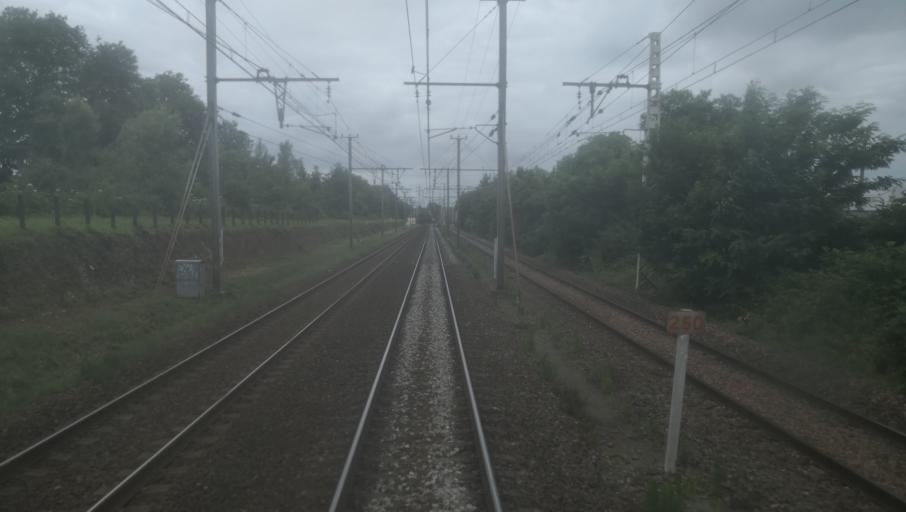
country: FR
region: Midi-Pyrenees
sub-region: Departement de la Haute-Garonne
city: Aucamville
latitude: 43.6614
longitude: 1.4160
